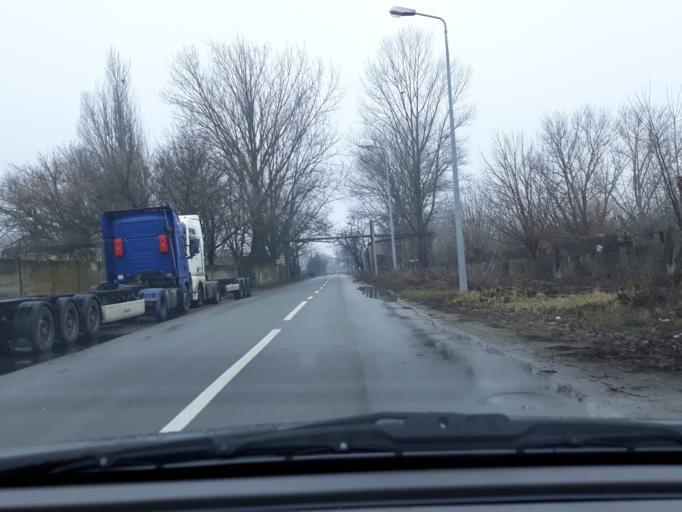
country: RO
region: Bihor
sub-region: Comuna Sanmartin
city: Sanmartin
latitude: 47.0371
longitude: 21.9651
